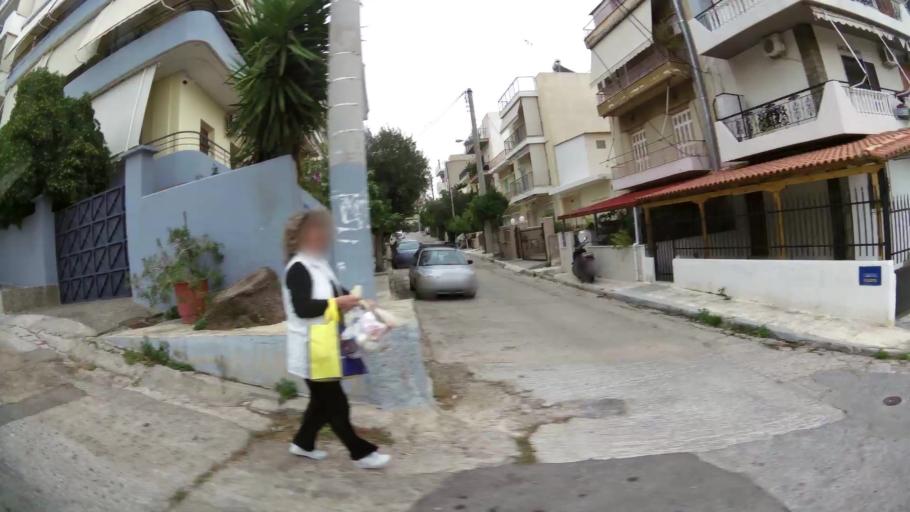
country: GR
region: Attica
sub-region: Nomos Piraios
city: Keratsini
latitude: 37.9782
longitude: 23.6248
